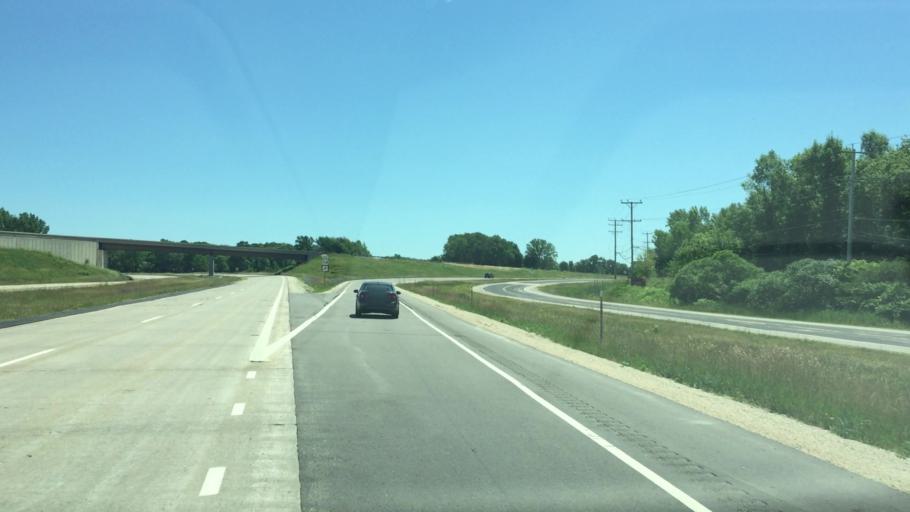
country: US
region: Wisconsin
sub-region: Outagamie County
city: Combined Locks
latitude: 44.2073
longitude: -88.3371
